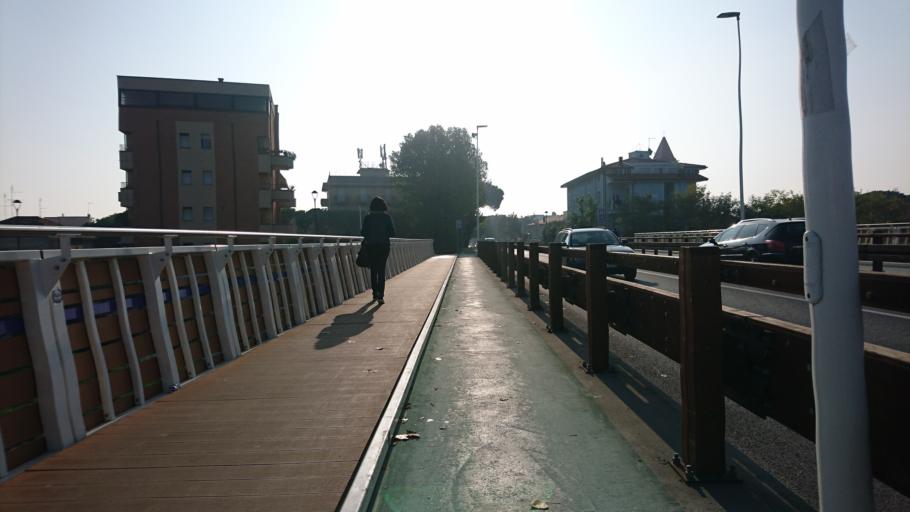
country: IT
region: Emilia-Romagna
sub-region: Provincia di Rimini
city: Rimini
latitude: 44.0731
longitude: 12.5612
